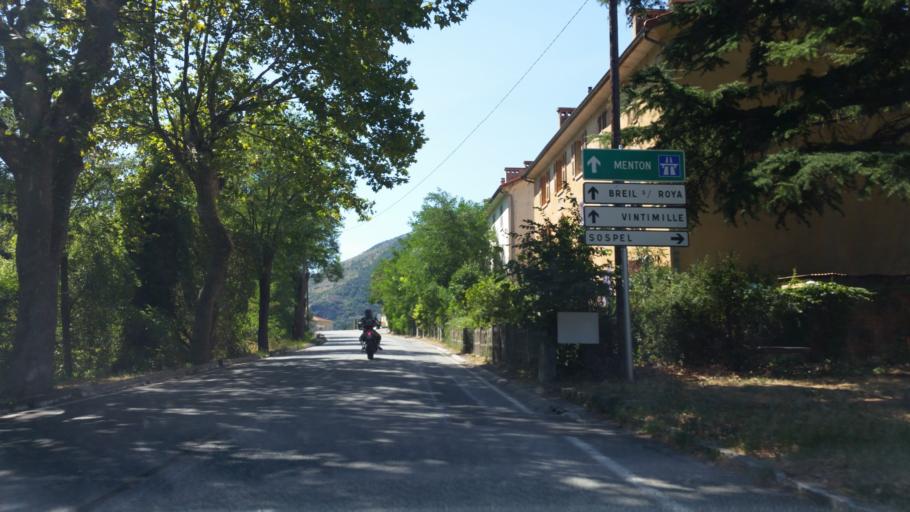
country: FR
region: Provence-Alpes-Cote d'Azur
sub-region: Departement des Alpes-Maritimes
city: Breil-sur-Roya
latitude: 43.9520
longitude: 7.5190
